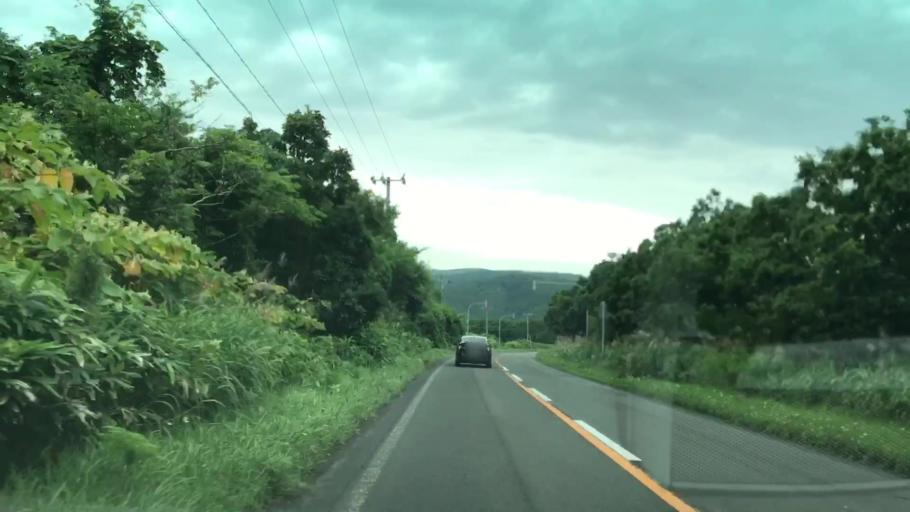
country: JP
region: Hokkaido
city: Iwanai
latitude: 42.8839
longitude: 140.3732
